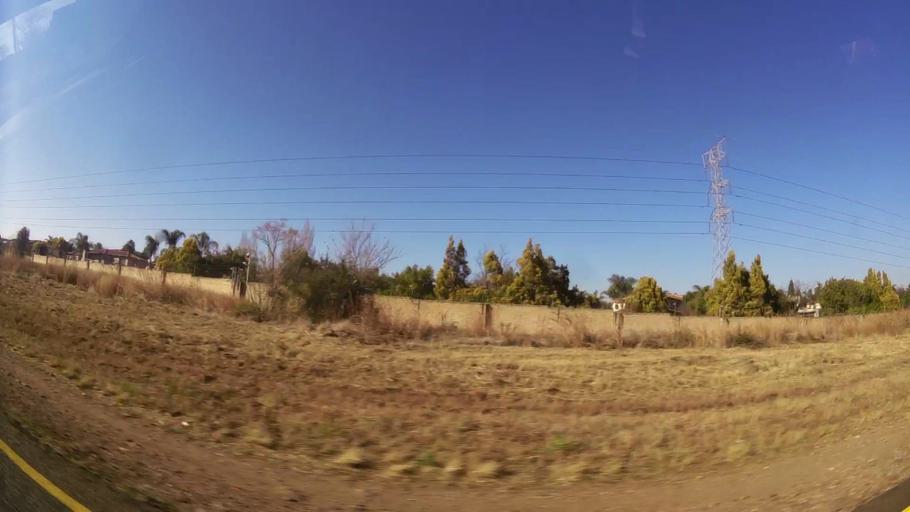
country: ZA
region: Gauteng
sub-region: City of Tshwane Metropolitan Municipality
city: Centurion
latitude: -25.8331
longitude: 28.1376
